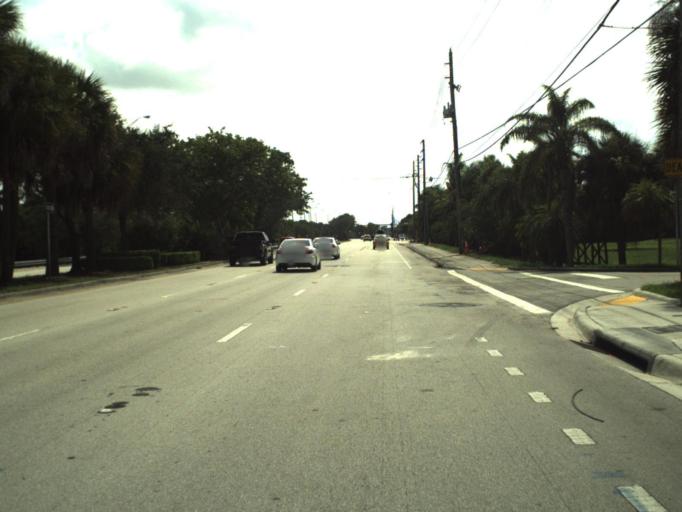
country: US
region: Florida
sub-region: Broward County
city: Davie
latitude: 26.0647
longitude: -80.2419
